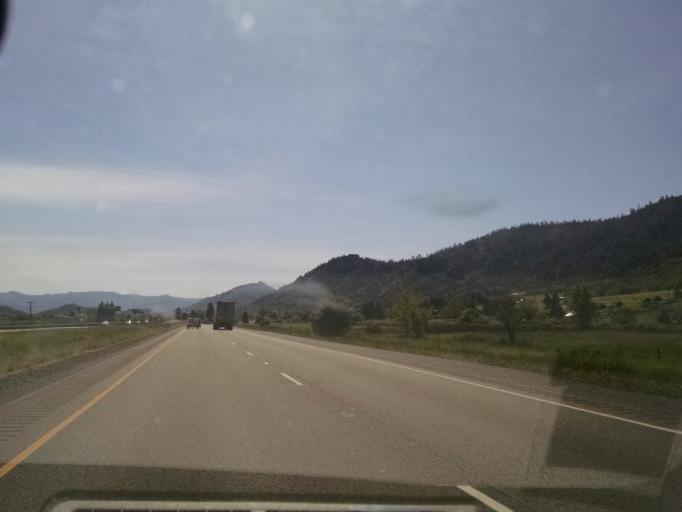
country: US
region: Oregon
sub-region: Douglas County
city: Tri-City
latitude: 43.0027
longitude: -123.3133
